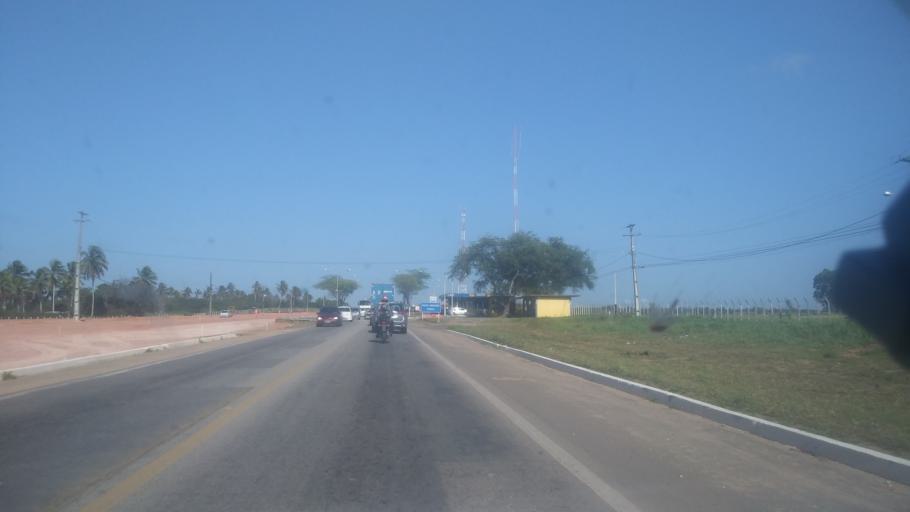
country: BR
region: Rio Grande do Norte
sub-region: Macaiba
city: Macaiba
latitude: -5.8675
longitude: -35.3691
